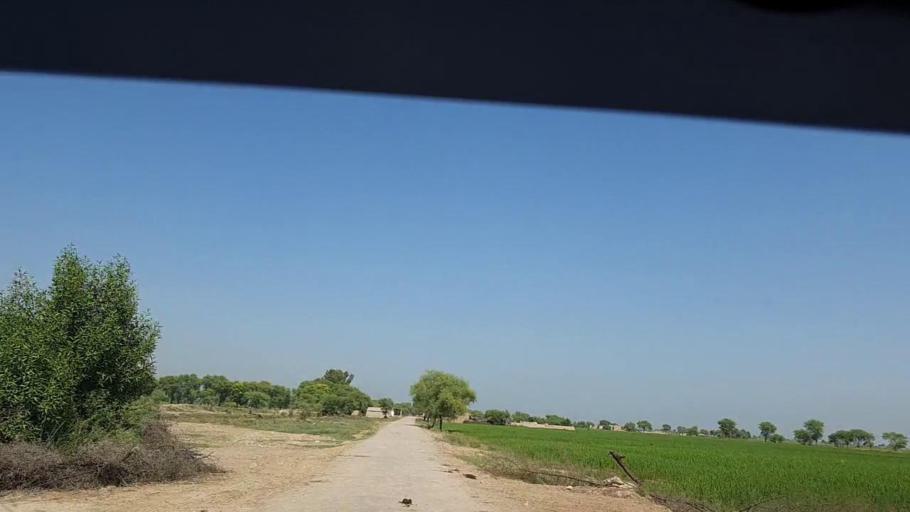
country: PK
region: Sindh
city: Tangwani
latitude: 28.2927
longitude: 69.0899
